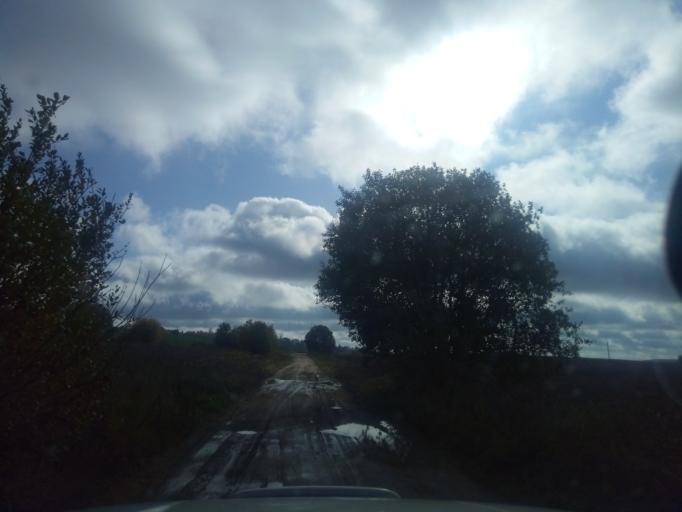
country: BY
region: Minsk
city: Zaslawye
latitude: 54.0223
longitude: 27.2879
